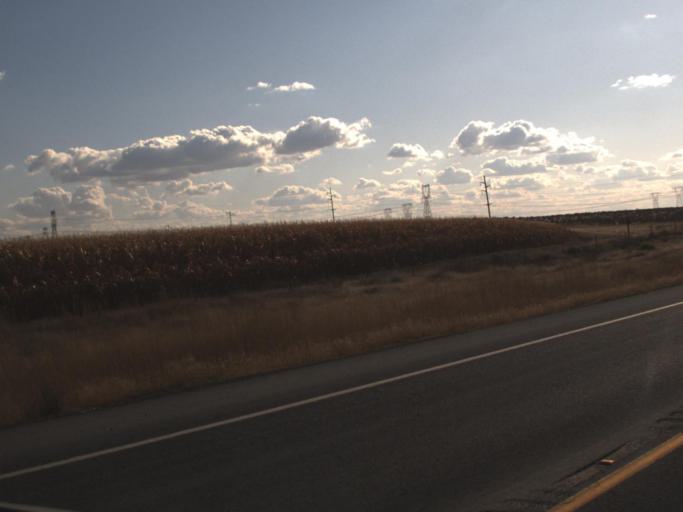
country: US
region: Oregon
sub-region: Morrow County
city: Irrigon
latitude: 45.9504
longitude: -119.4328
